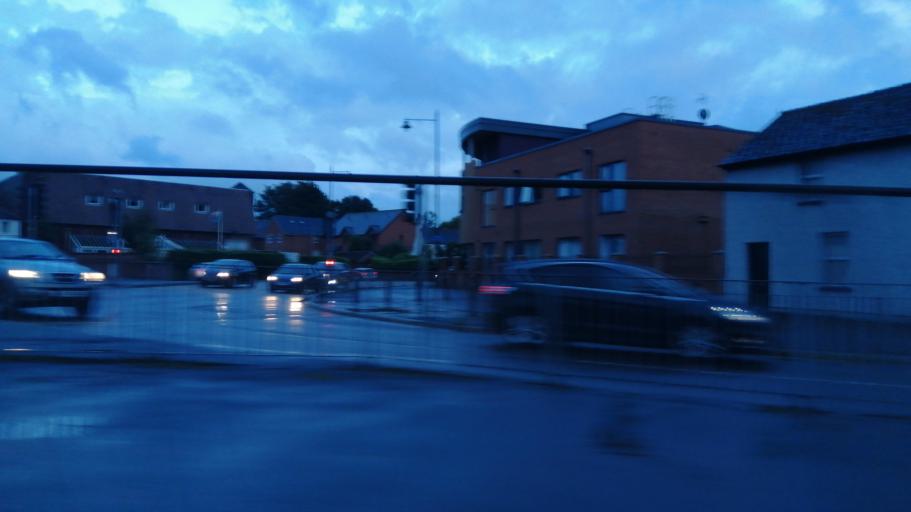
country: GB
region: England
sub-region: Herefordshire
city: Hereford
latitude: 52.0488
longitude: -2.7199
